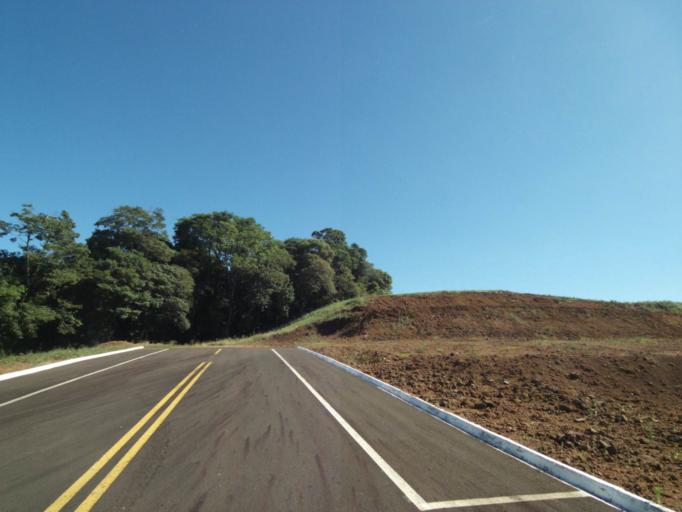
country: BR
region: Parana
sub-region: Pato Branco
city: Pato Branco
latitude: -26.2629
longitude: -52.7742
